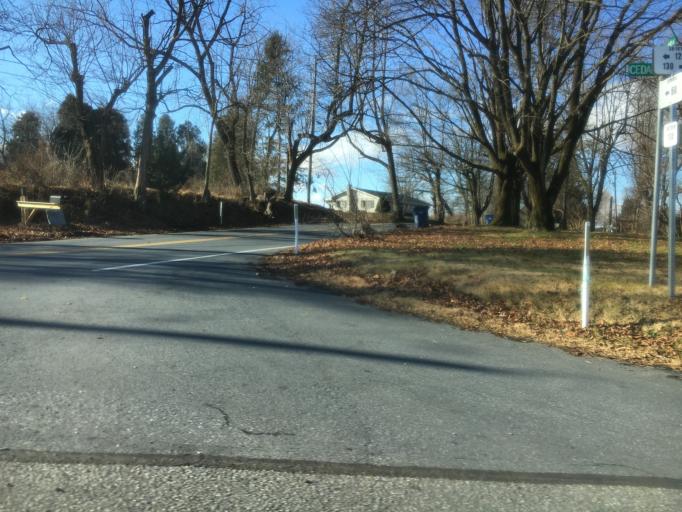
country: US
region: Pennsylvania
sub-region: Lehigh County
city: Egypt
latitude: 40.6470
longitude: -75.5486
